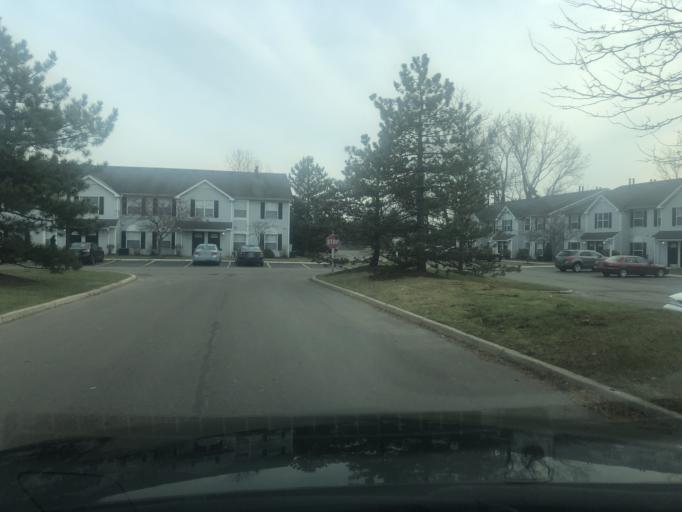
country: US
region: Michigan
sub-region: Wayne County
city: Belleville
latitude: 42.2165
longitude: -83.4930
